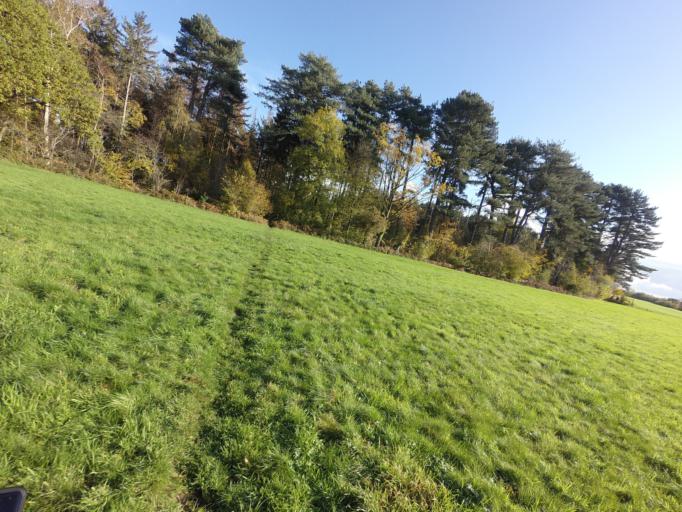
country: BE
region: Wallonia
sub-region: Province de Liege
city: Aubel
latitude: 50.7580
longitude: 5.8888
